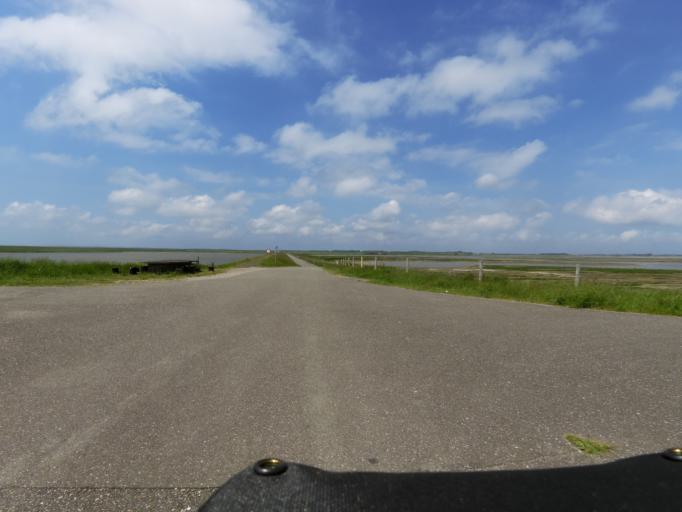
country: NL
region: Zeeland
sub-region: Schouwen-Duiveland
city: Scharendijke
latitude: 51.6833
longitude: 3.8390
